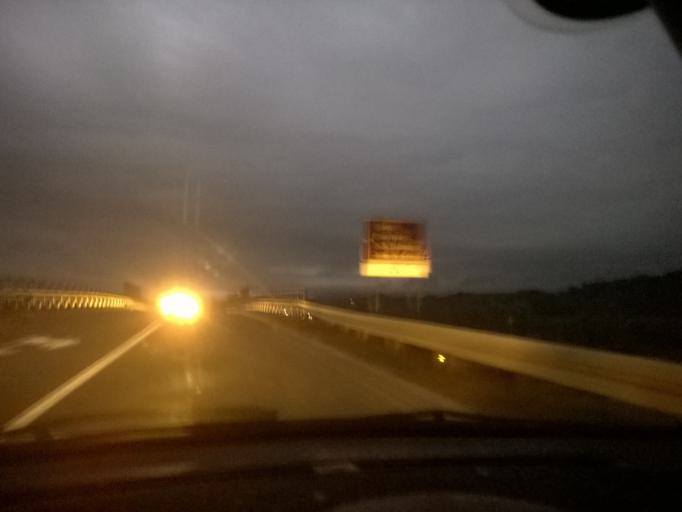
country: HR
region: Krapinsko-Zagorska
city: Zabok
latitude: 46.0255
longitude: 15.9118
